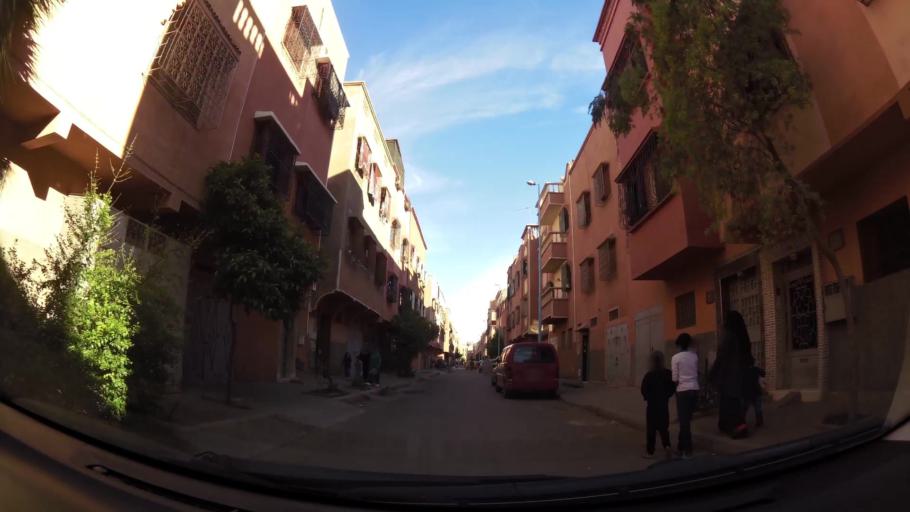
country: MA
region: Marrakech-Tensift-Al Haouz
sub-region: Marrakech
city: Marrakesh
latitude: 31.6215
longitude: -8.0685
